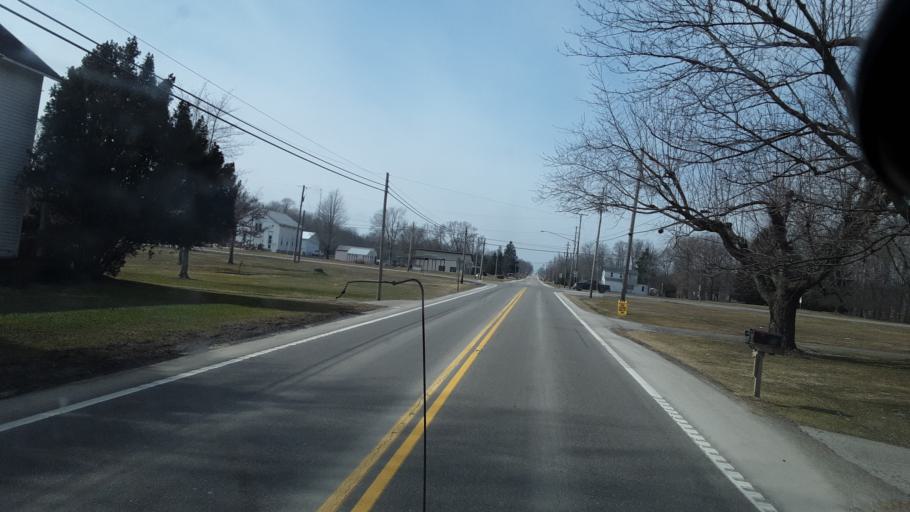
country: US
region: Ohio
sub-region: Ashtabula County
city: Andover
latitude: 41.6070
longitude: -80.6652
